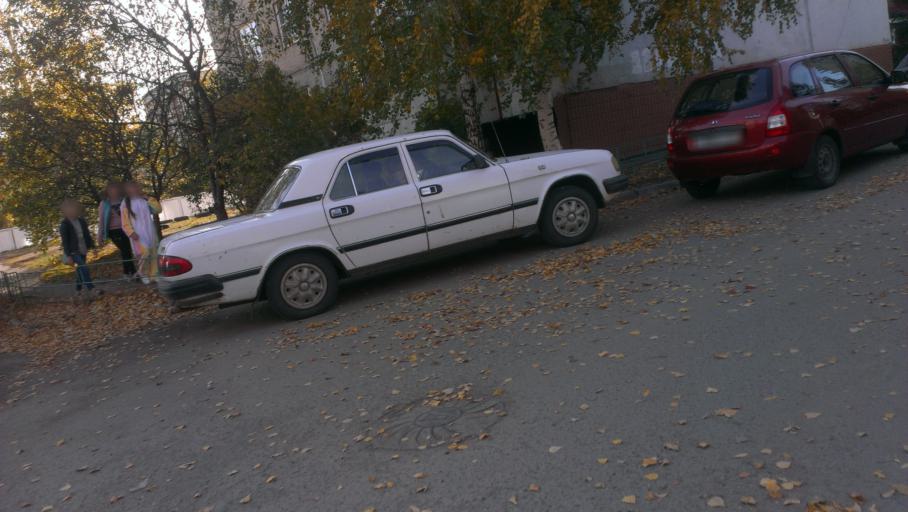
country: RU
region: Altai Krai
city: Novosilikatnyy
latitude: 53.3335
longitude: 83.6819
